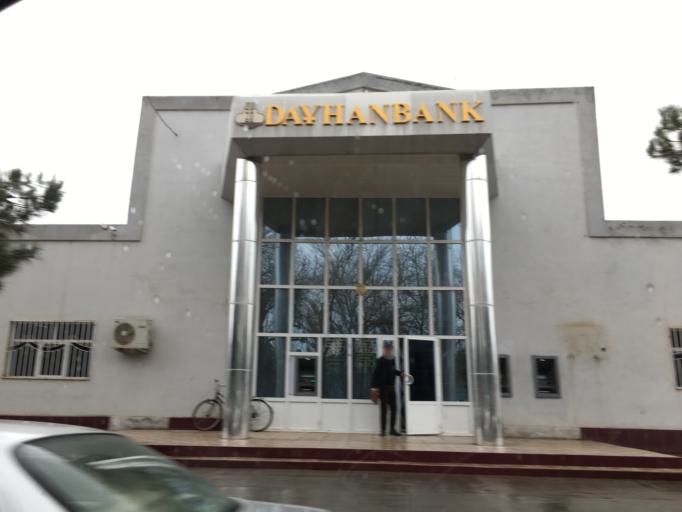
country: TM
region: Mary
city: Yoloeten
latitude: 37.3003
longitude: 62.3582
